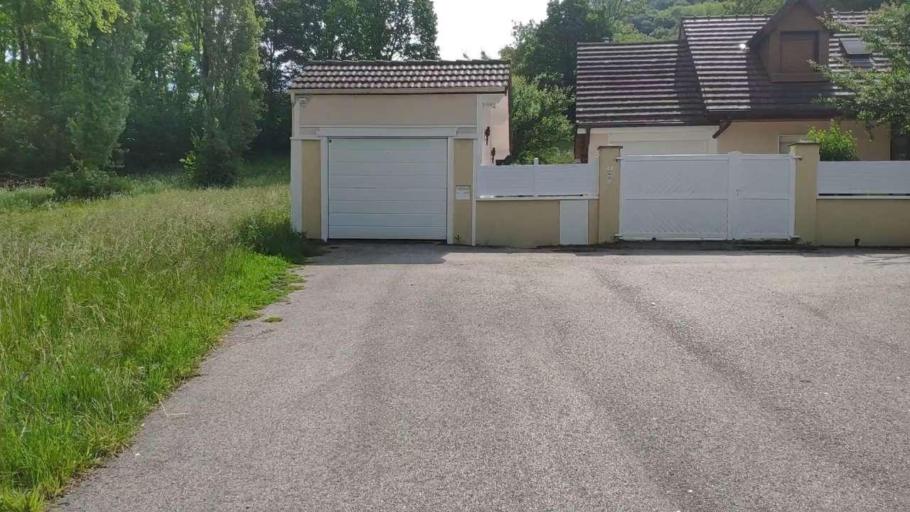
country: FR
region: Franche-Comte
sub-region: Departement du Jura
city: Perrigny
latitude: 46.7574
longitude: 5.6170
